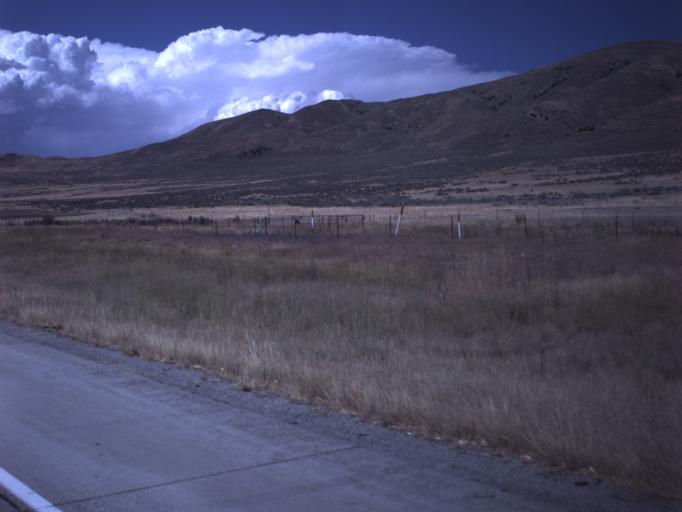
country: US
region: Utah
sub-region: Box Elder County
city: Garland
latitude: 41.7556
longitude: -112.2604
